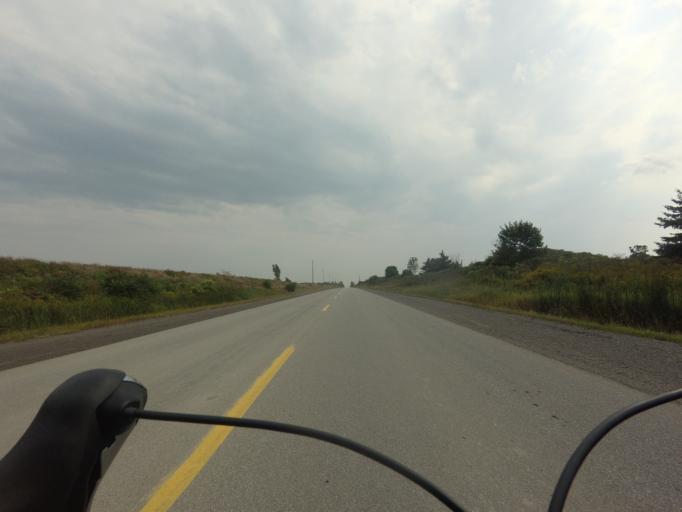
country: CA
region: Ontario
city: Bells Corners
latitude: 45.2386
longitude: -75.7553
